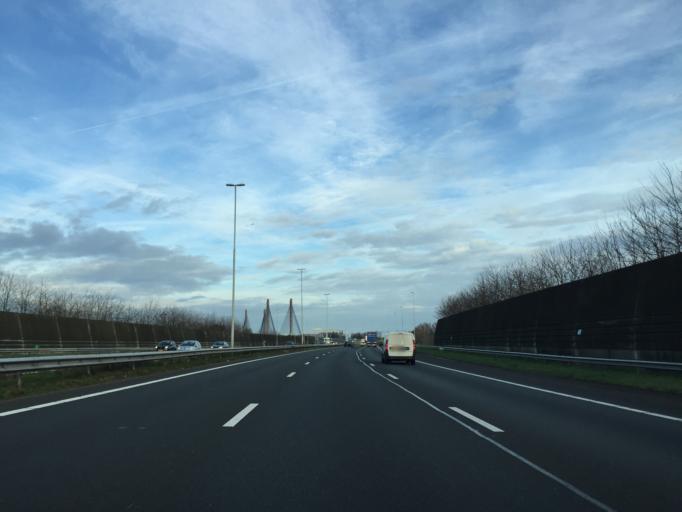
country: NL
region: Gelderland
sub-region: Gemeente Zaltbommel
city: Zaltbommel
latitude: 51.8087
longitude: 5.2593
